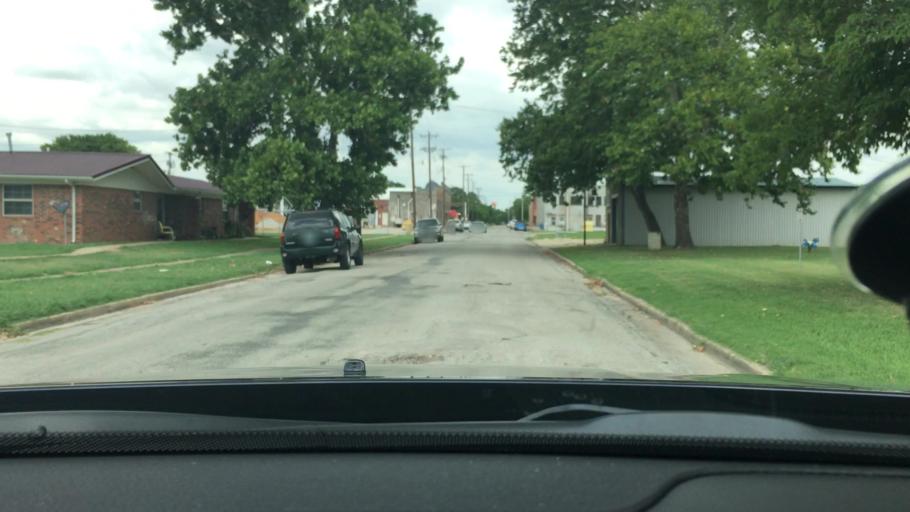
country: US
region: Oklahoma
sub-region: Love County
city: Marietta
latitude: 33.9354
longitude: -97.1194
